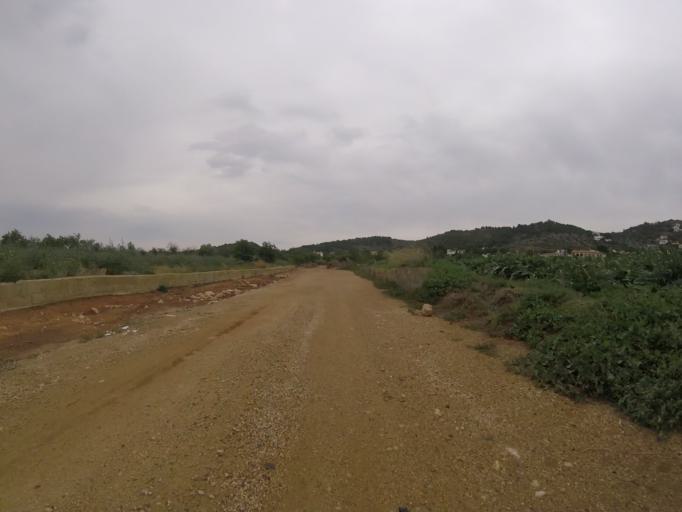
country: ES
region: Valencia
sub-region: Provincia de Castello
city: Alcoceber
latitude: 40.2451
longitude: 0.2588
